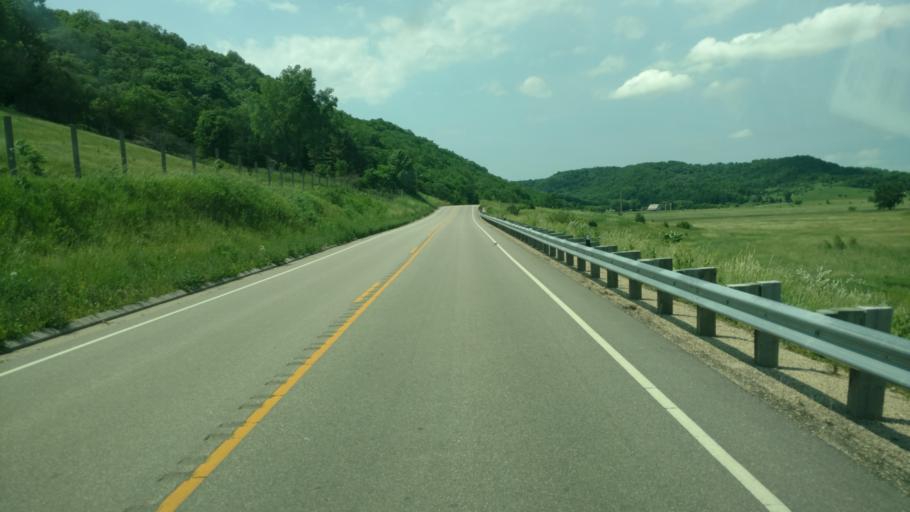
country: US
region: Wisconsin
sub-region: Vernon County
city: Viroqua
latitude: 43.5163
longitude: -90.6623
